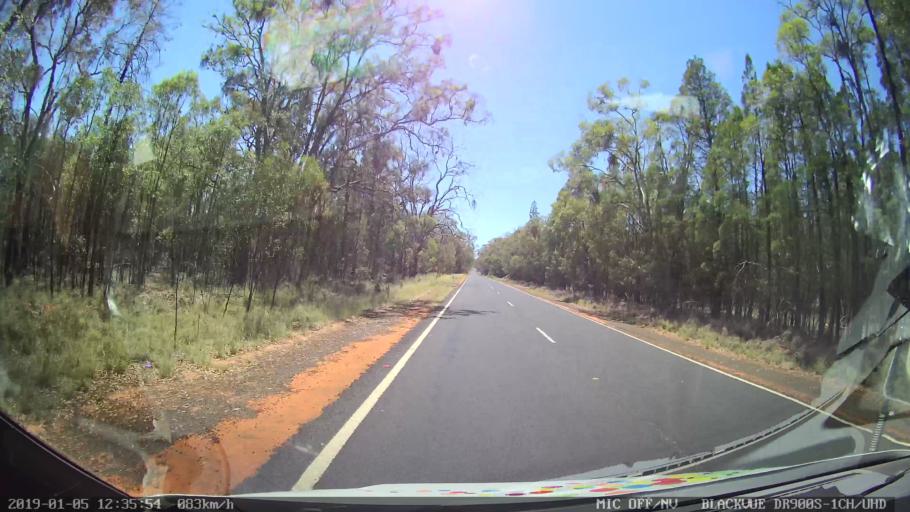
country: AU
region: New South Wales
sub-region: Warrumbungle Shire
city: Coonabarabran
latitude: -31.2085
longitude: 149.4325
